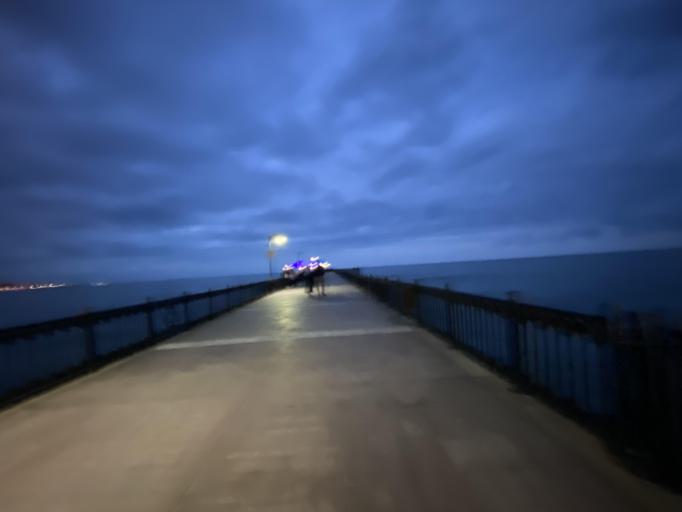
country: TR
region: Samsun
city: Samsun
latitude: 41.3442
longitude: 36.2619
